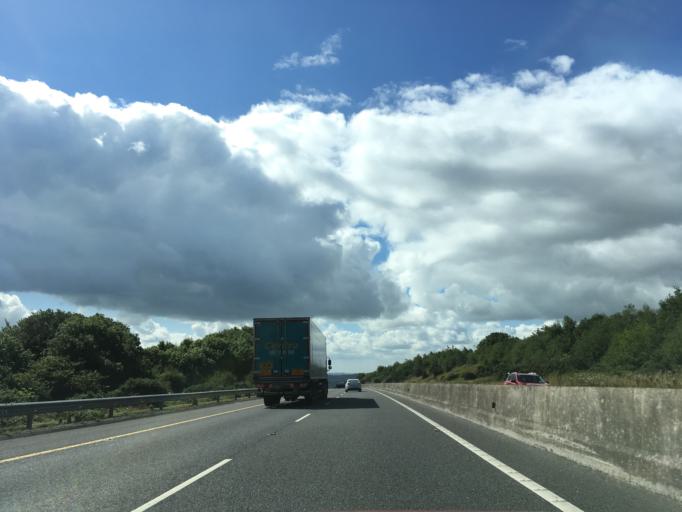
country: IE
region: Munster
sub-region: County Cork
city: Mitchelstown
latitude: 52.2018
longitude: -8.2742
